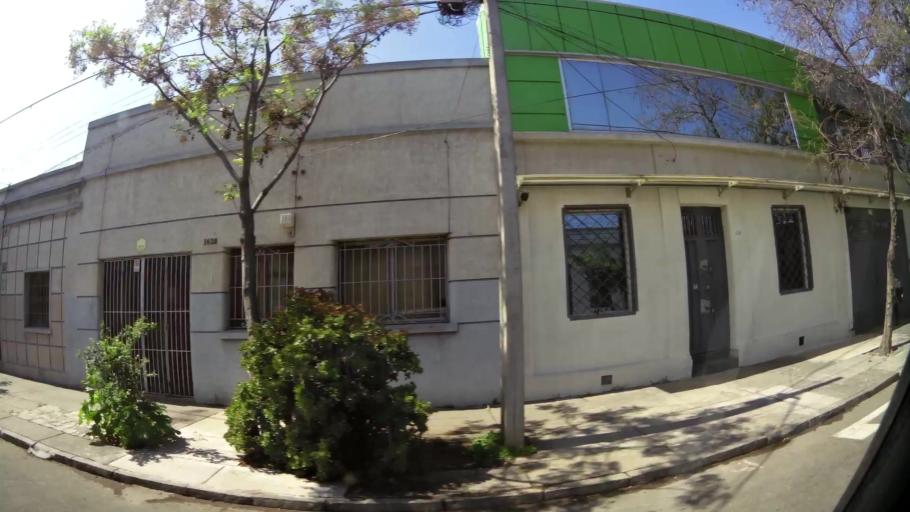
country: CL
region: Santiago Metropolitan
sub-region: Provincia de Santiago
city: Santiago
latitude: -33.4626
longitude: -70.6341
